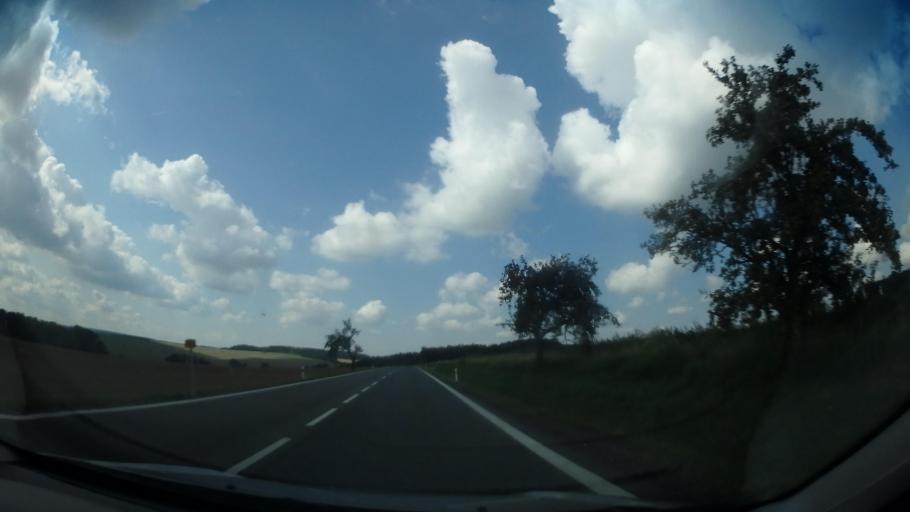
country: CZ
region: Central Bohemia
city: Kostelec nad Cernymi Lesy
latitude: 49.9738
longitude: 14.9047
